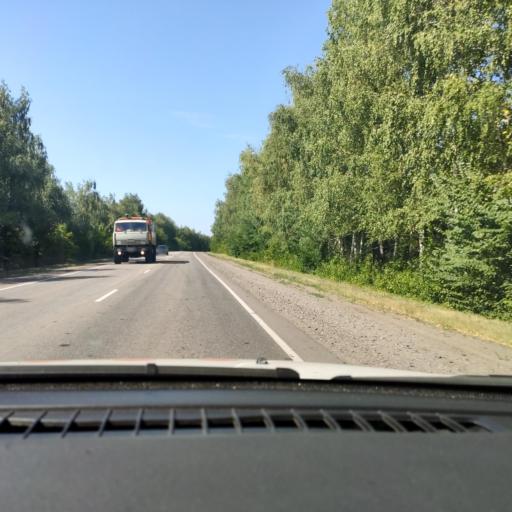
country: RU
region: Voronezj
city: Imeni Pervogo Maya
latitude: 50.7381
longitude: 39.3892
